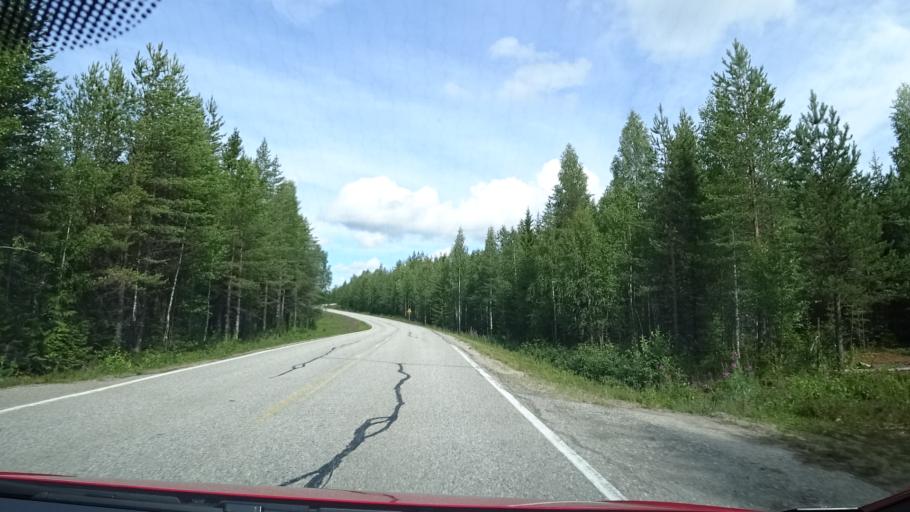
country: FI
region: Kainuu
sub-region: Kehys-Kainuu
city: Kuhmo
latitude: 64.4318
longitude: 29.8110
